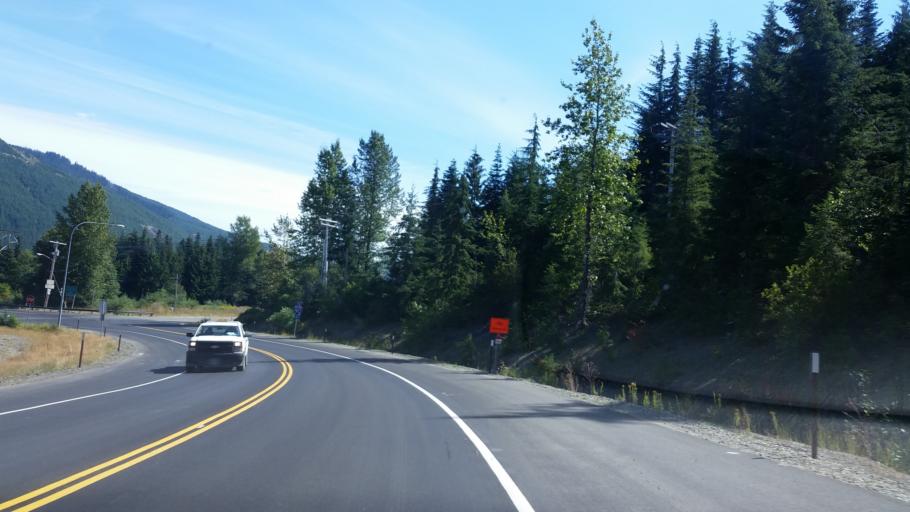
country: US
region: Washington
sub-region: King County
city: Tanner
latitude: 47.3958
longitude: -121.3994
